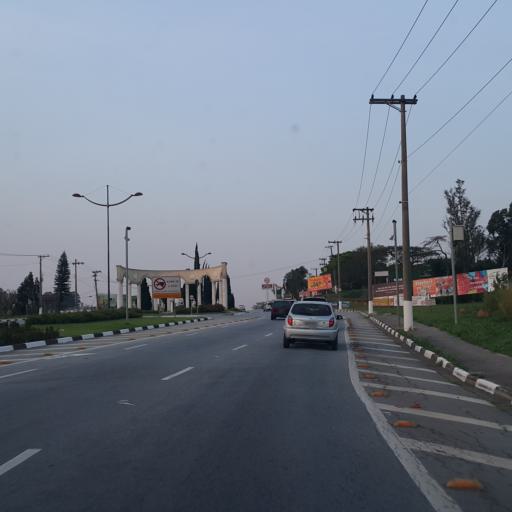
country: BR
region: Sao Paulo
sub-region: Vinhedo
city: Vinhedo
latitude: -23.0589
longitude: -46.9920
